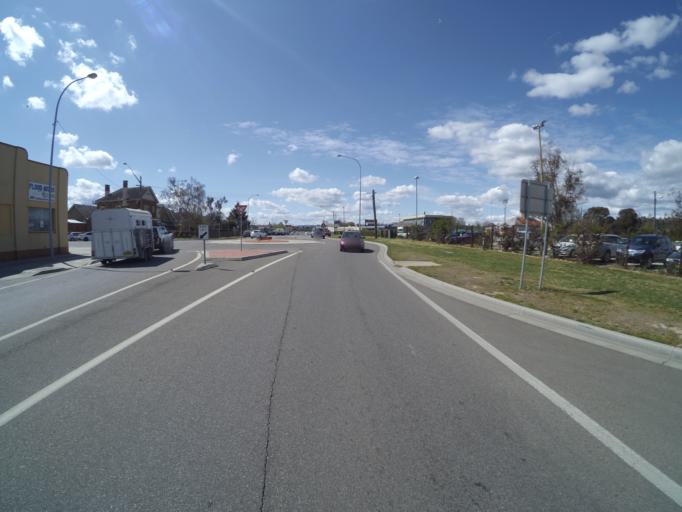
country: AU
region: New South Wales
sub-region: Goulburn Mulwaree
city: Goulburn
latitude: -34.7528
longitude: 149.7231
